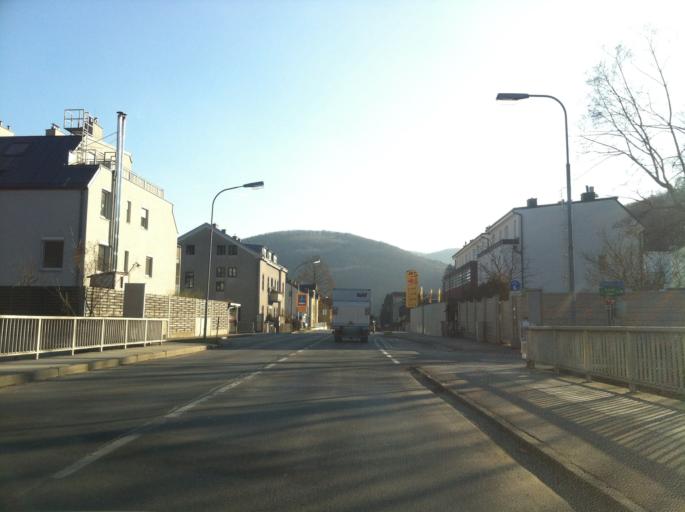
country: AT
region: Lower Austria
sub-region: Politischer Bezirk Wien-Umgebung
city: Purkersdorf
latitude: 48.2126
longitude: 16.1723
